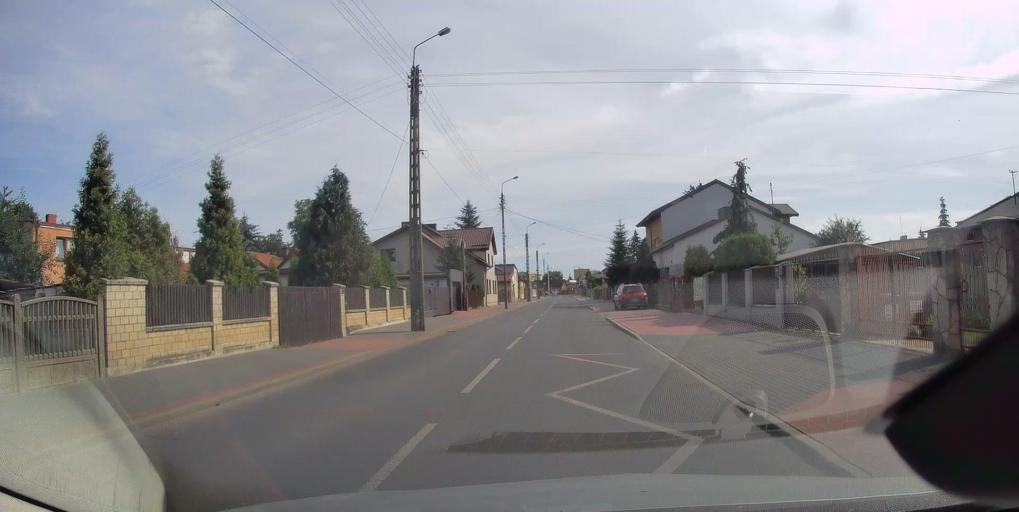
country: PL
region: Lodz Voivodeship
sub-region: Powiat tomaszowski
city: Tomaszow Mazowiecki
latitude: 51.5270
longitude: 19.9974
